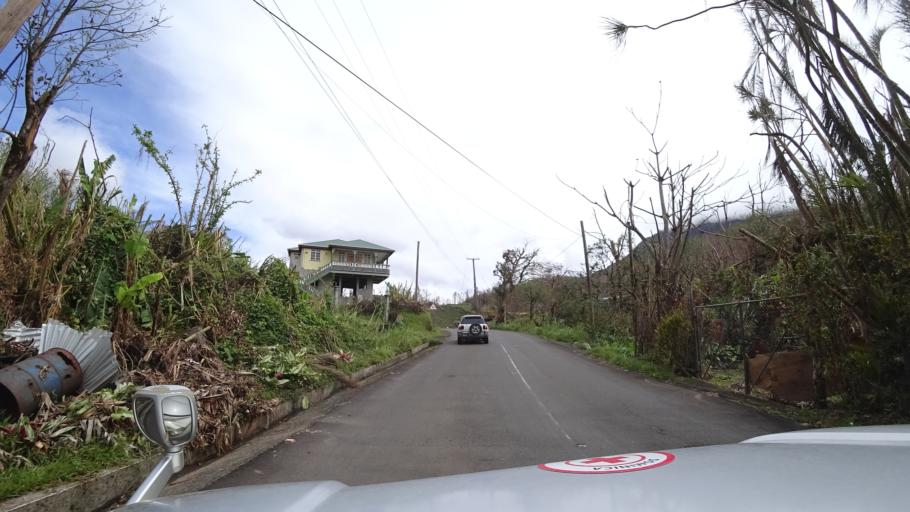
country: DM
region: Saint Paul
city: Pont Casse
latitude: 15.3599
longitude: -61.3551
